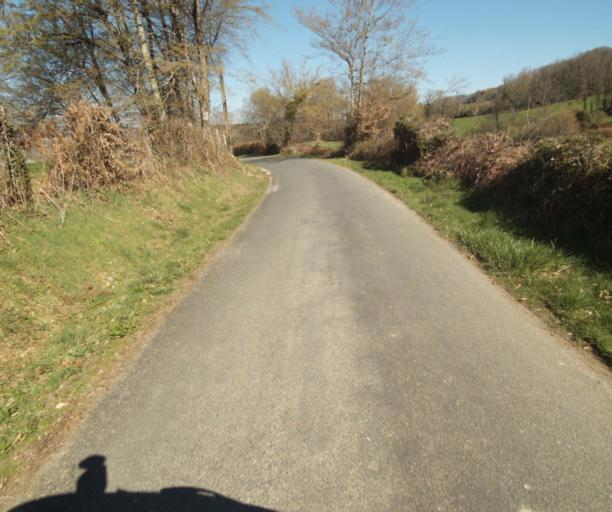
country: FR
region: Limousin
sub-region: Departement de la Correze
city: Saint-Mexant
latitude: 45.3094
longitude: 1.6012
